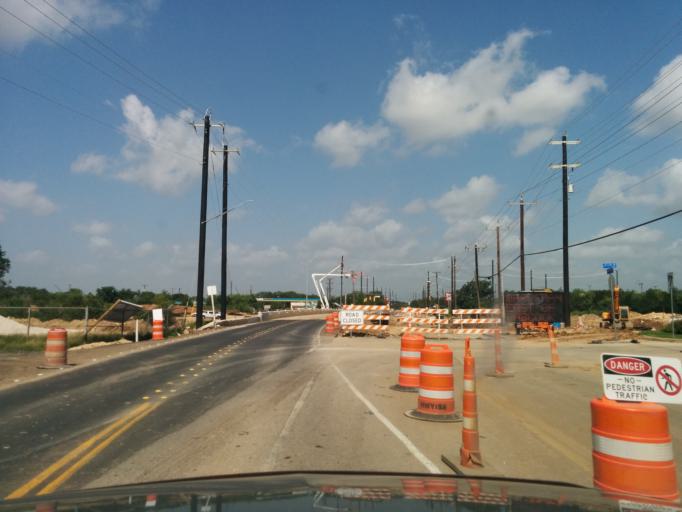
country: US
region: Texas
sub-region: Bexar County
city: Helotes
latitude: 29.5721
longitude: -98.6295
